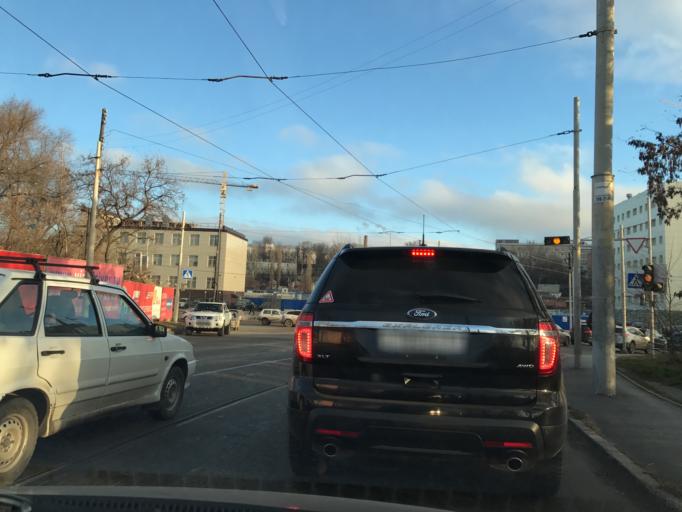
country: RU
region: Rostov
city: Rostov-na-Donu
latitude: 47.2239
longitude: 39.6858
